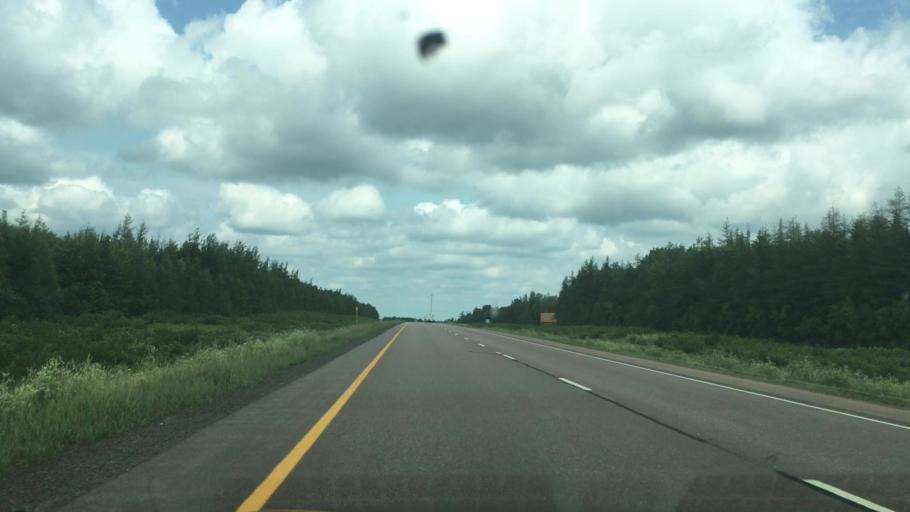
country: CA
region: New Brunswick
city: Dieppe
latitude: 46.0602
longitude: -64.5875
